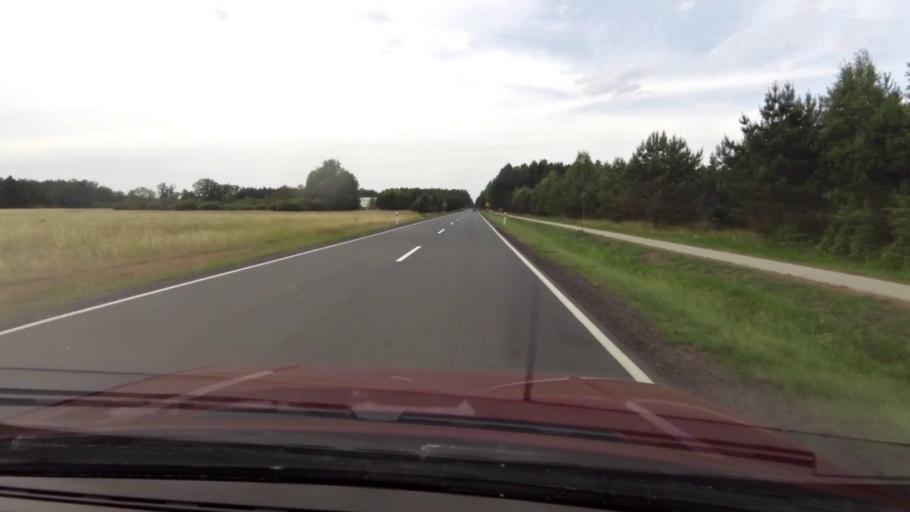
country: PL
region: Pomeranian Voivodeship
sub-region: Powiat bytowski
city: Trzebielino
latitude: 54.2132
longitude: 17.0892
